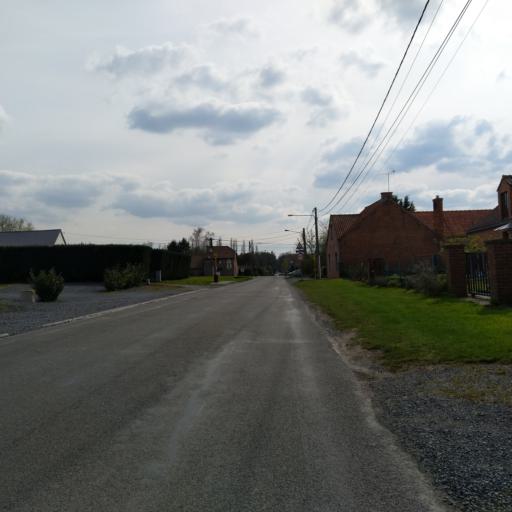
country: BE
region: Wallonia
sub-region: Province du Hainaut
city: Jurbise
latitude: 50.5098
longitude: 3.9578
